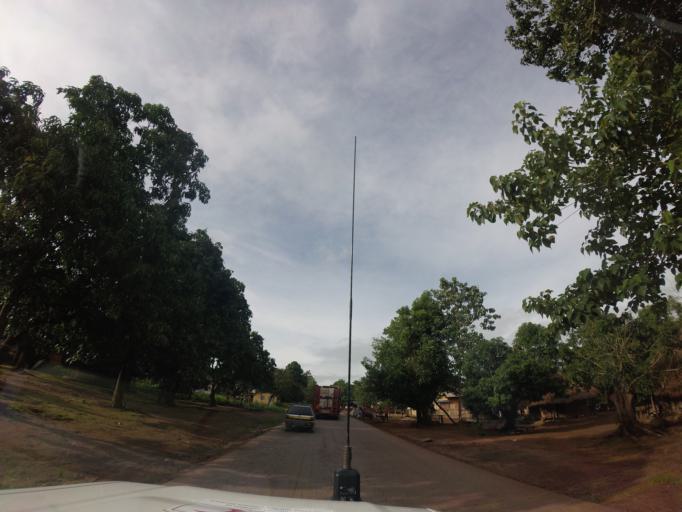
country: GN
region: Kindia
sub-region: Kindia
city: Kindia
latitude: 9.9144
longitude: -12.9964
